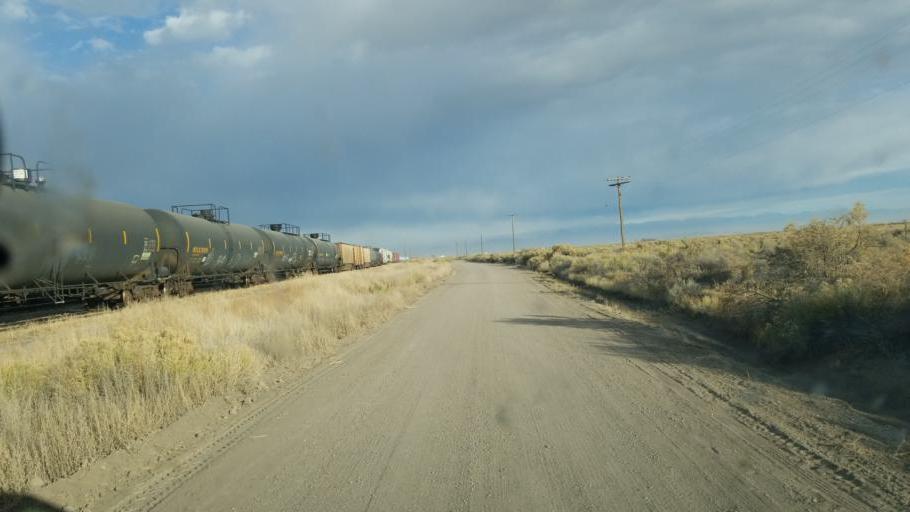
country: US
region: Colorado
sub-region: Alamosa County
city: Alamosa East
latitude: 37.4655
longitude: -105.8390
